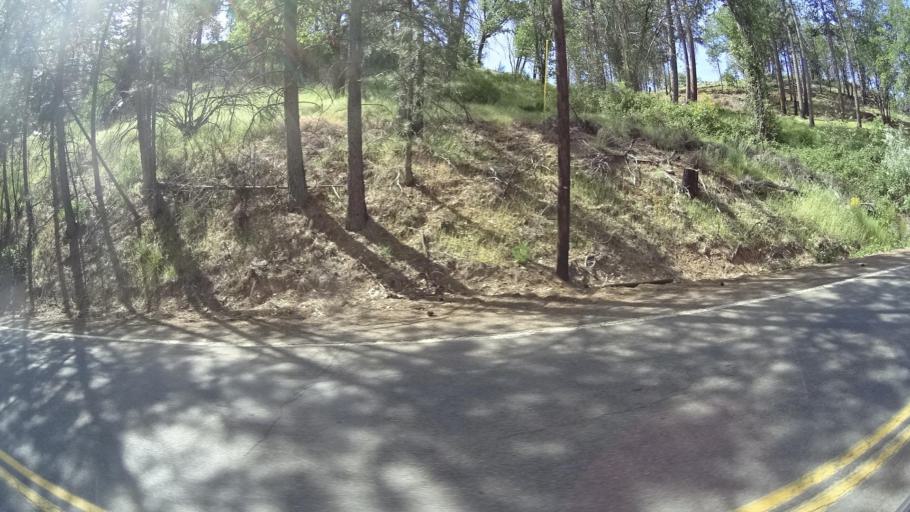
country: US
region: California
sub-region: Lake County
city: Cobb
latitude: 38.8571
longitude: -122.7499
